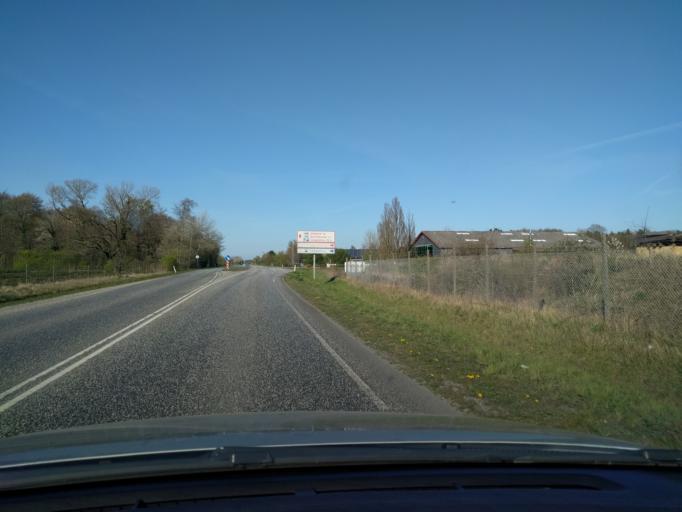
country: DK
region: South Denmark
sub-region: Kerteminde Kommune
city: Langeskov
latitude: 55.3564
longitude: 10.5826
